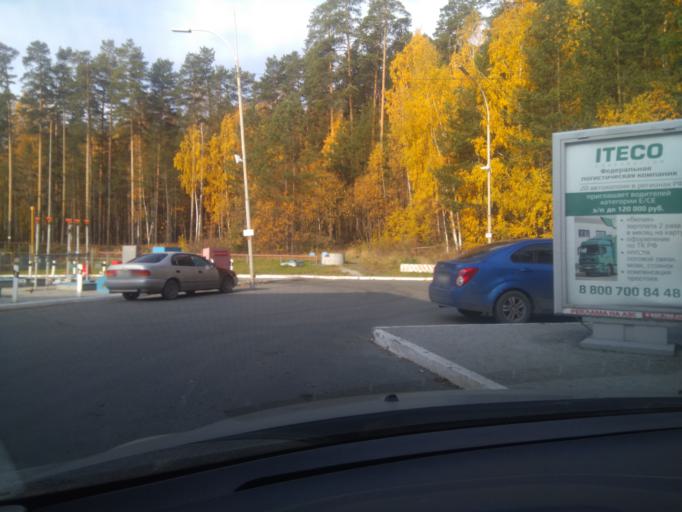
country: RU
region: Sverdlovsk
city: Shirokaya Rechka
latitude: 56.8264
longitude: 60.4682
